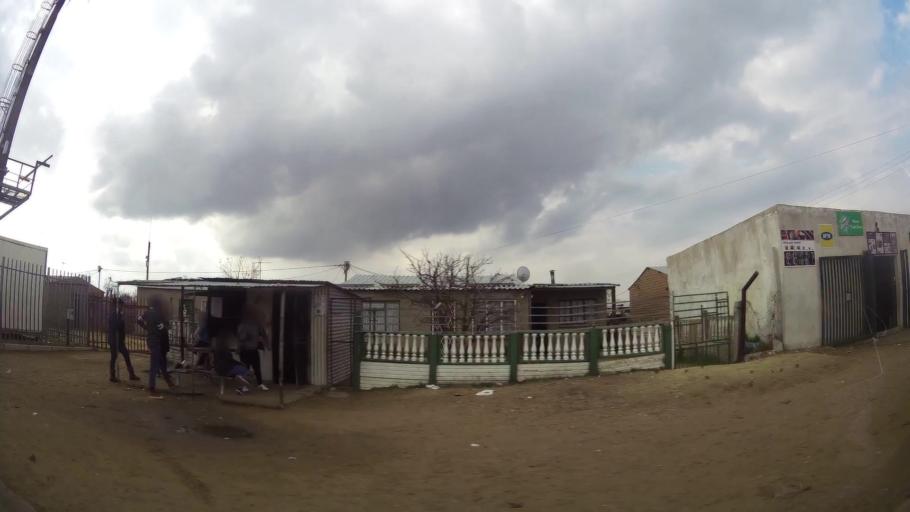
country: ZA
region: Orange Free State
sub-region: Fezile Dabi District Municipality
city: Sasolburg
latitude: -26.8570
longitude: 27.8574
